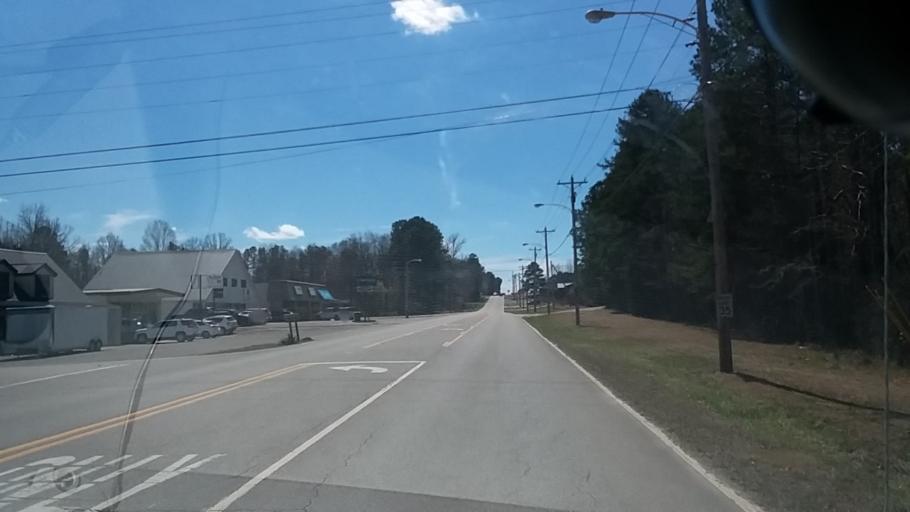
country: US
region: Mississippi
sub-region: Tishomingo County
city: Iuka
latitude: 34.8025
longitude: -88.2038
